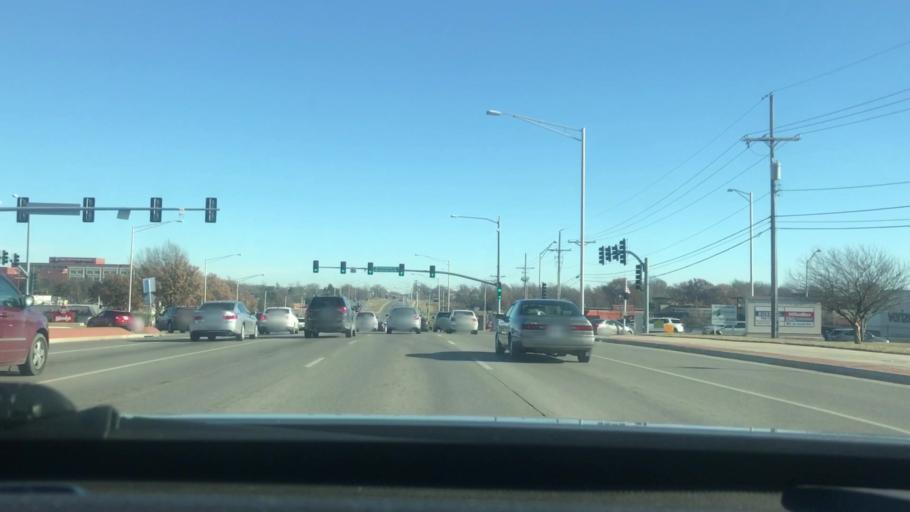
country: US
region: Missouri
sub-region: Platte County
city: Weatherby Lake
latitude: 39.2468
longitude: -94.6558
